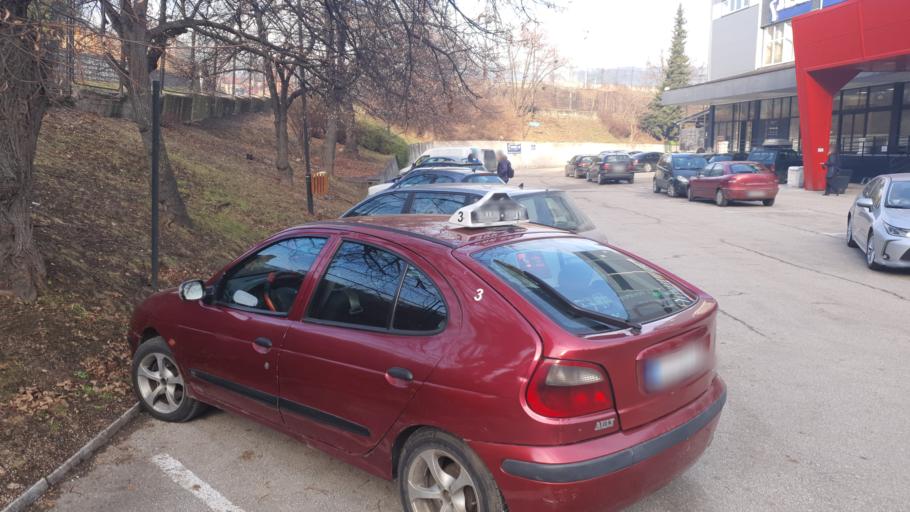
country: RS
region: Central Serbia
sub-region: Zlatiborski Okrug
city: Uzice
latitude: 43.8482
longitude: 19.8524
